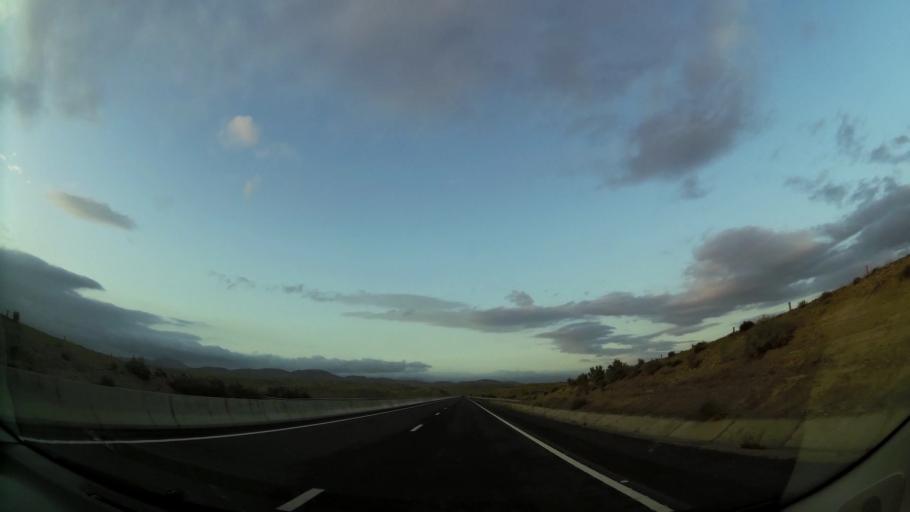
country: MA
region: Oriental
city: Taourirt
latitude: 34.5625
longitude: -2.8357
